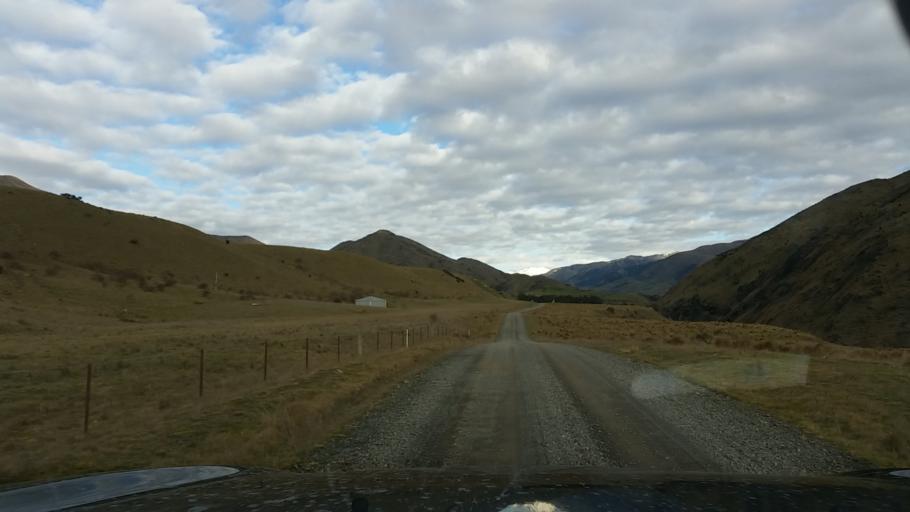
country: NZ
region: Marlborough
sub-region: Marlborough District
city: Blenheim
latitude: -41.8813
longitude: 173.6491
